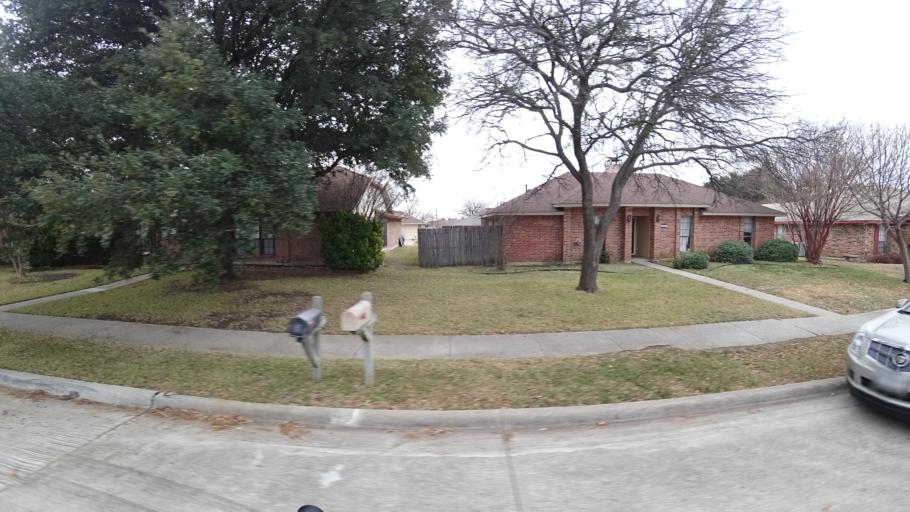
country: US
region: Texas
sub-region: Denton County
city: Lewisville
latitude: 33.0438
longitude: -97.0386
